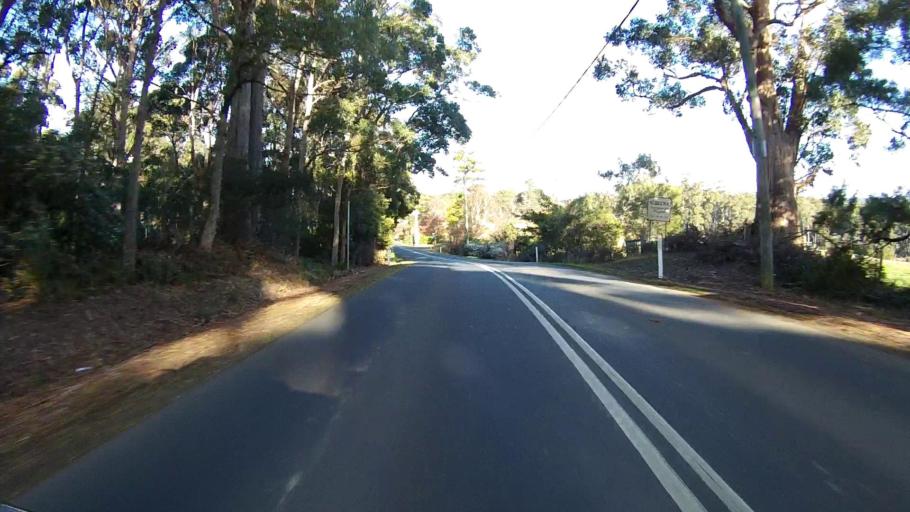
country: AU
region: Tasmania
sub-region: Clarence
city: Sandford
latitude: -43.1339
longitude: 147.8499
